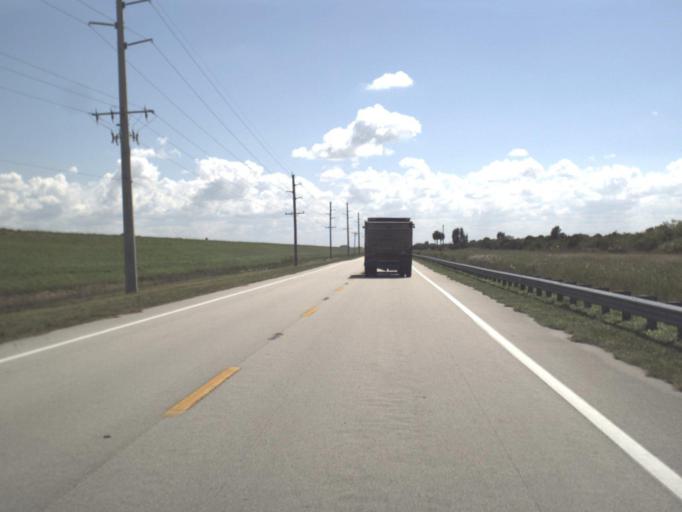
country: US
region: Florida
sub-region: Glades County
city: Moore Haven
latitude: 26.9039
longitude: -81.1225
